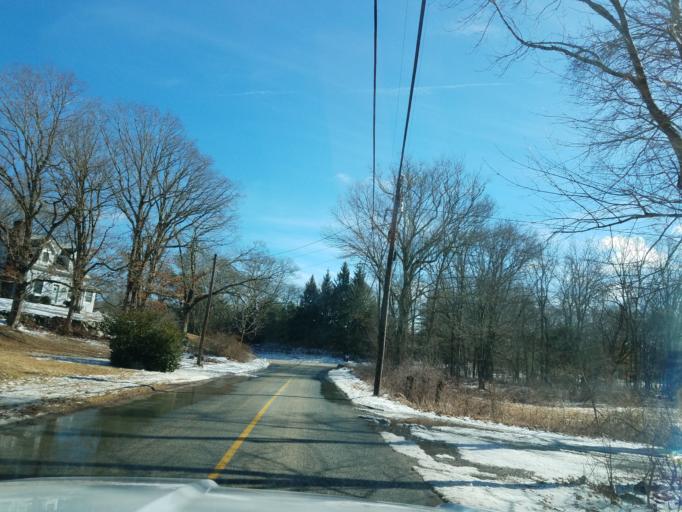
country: US
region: Connecticut
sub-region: New London County
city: Preston City
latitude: 41.4962
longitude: -71.9017
